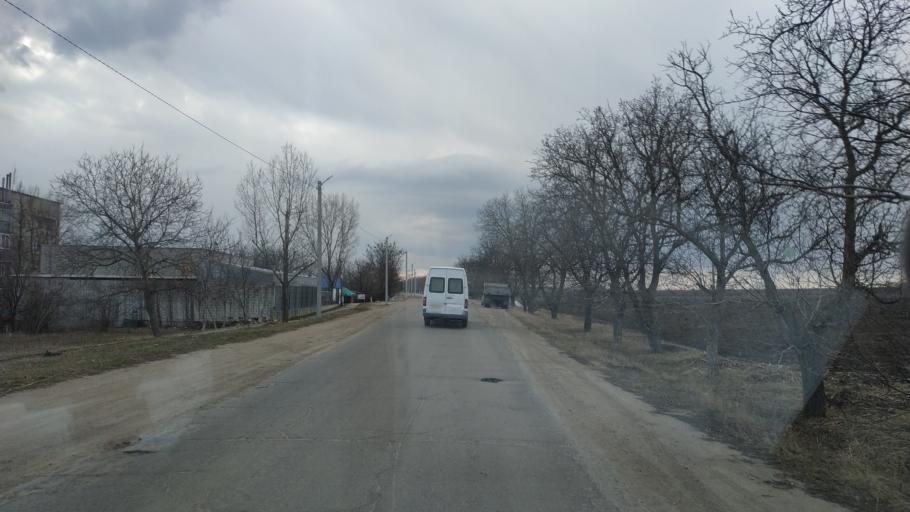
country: MD
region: Anenii Noi
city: Anenii Noi
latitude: 46.8997
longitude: 29.3106
